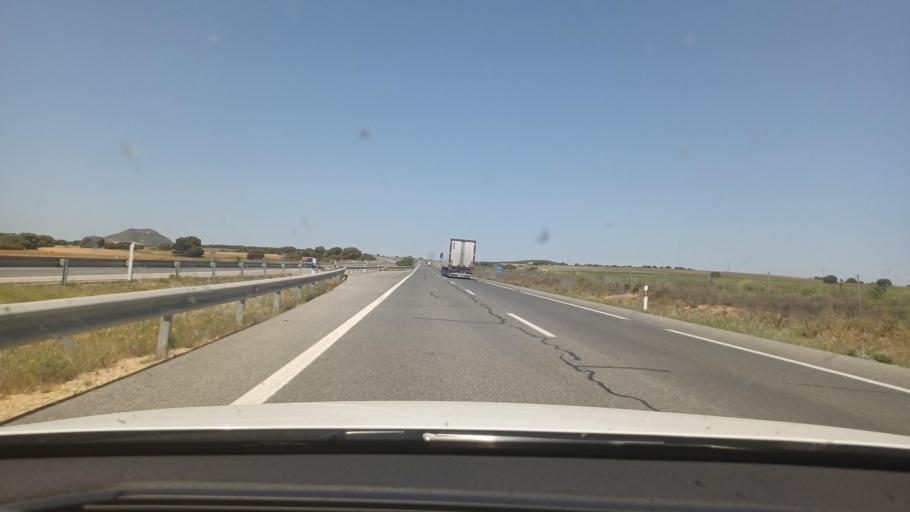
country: ES
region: Castille-La Mancha
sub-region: Provincia de Albacete
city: Corral-Rubio
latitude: 38.8939
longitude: -1.4217
